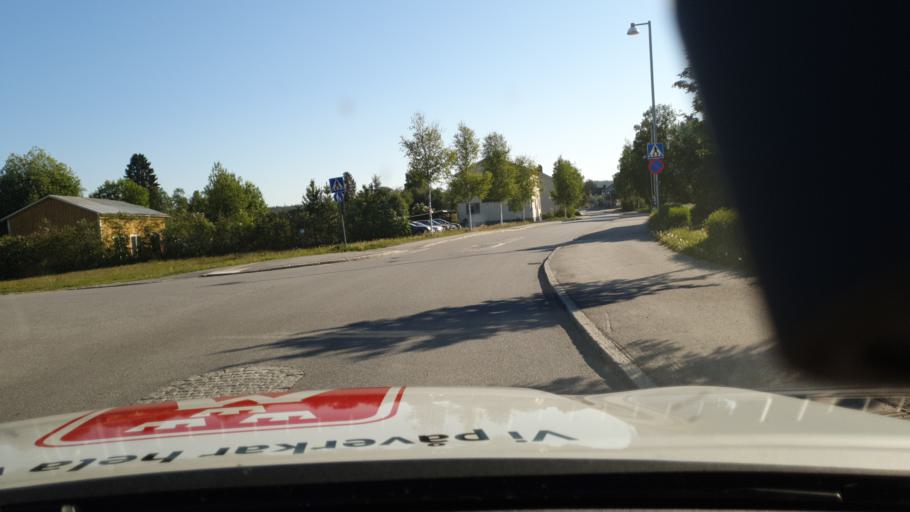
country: SE
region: Vaesterbotten
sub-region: Vindelns Kommun
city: Vindeln
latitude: 64.1979
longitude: 19.7133
